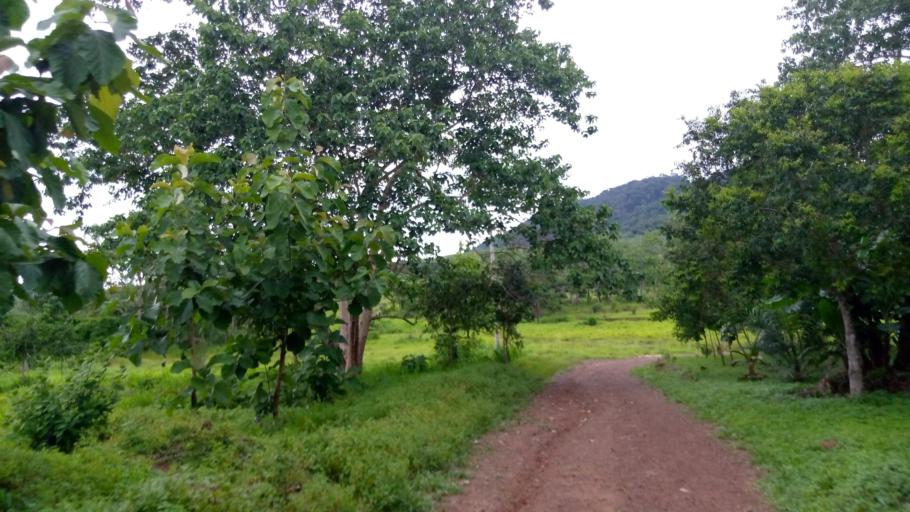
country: SL
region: Southern Province
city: Moyamba
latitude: 8.1582
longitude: -12.4480
